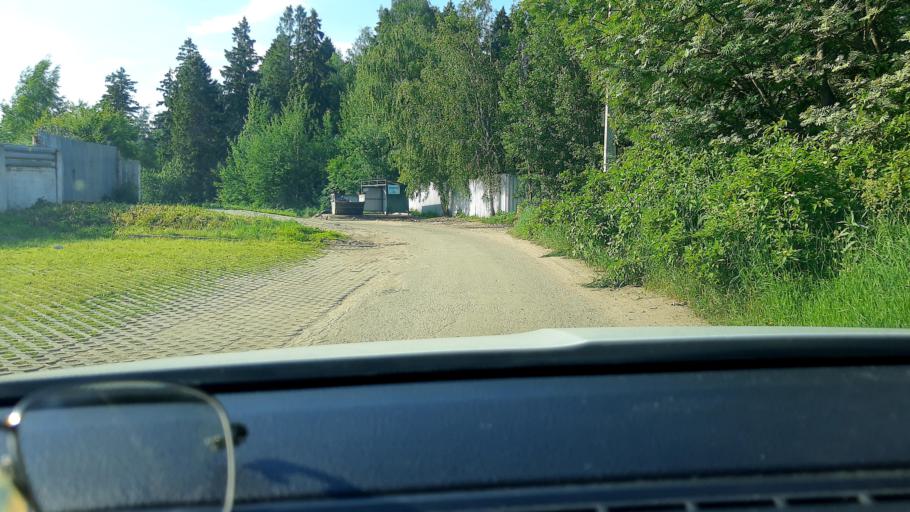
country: RU
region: Moscow
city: Novo-Peredelkino
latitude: 55.6681
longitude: 37.3227
